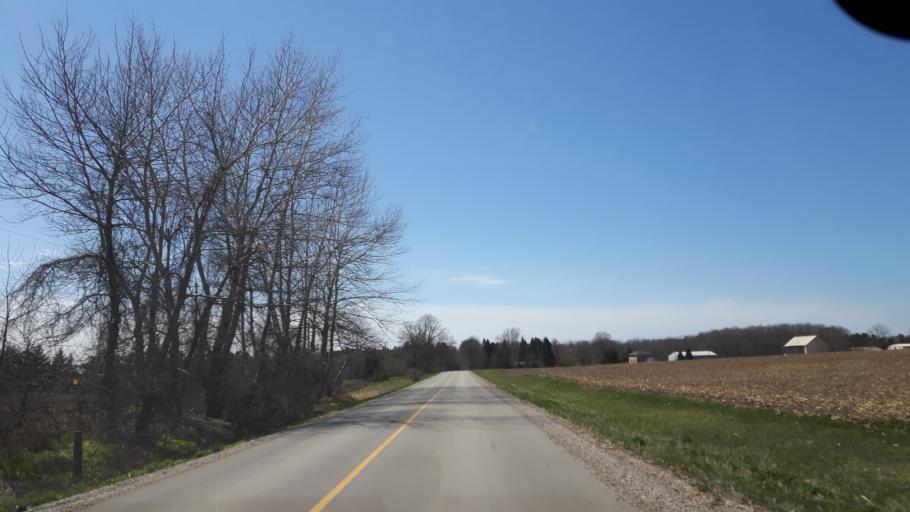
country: CA
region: Ontario
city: Bluewater
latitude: 43.5812
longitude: -81.6592
